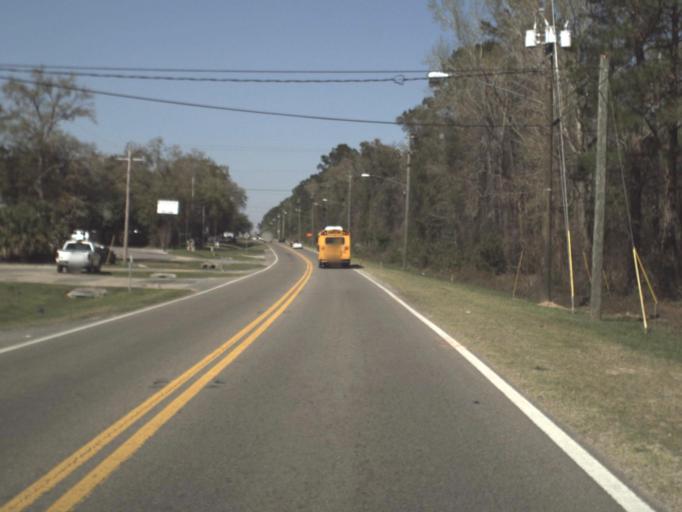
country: US
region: Florida
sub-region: Leon County
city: Tallahassee
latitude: 30.4428
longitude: -84.3476
